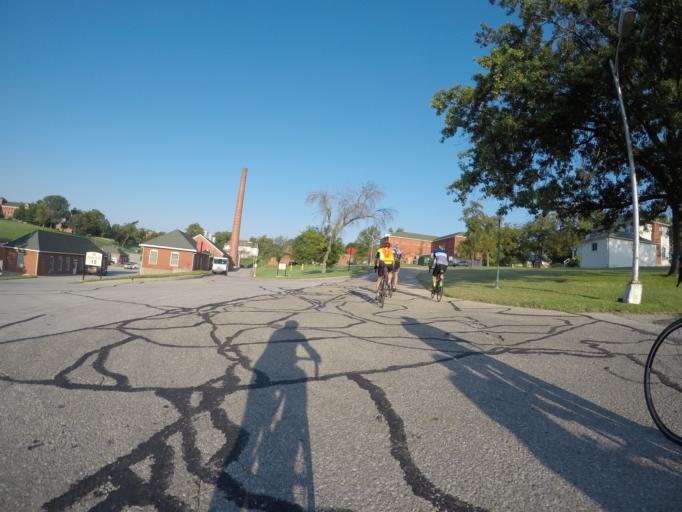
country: US
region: Kansas
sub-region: Leavenworth County
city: Lansing
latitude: 39.2799
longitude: -94.8922
